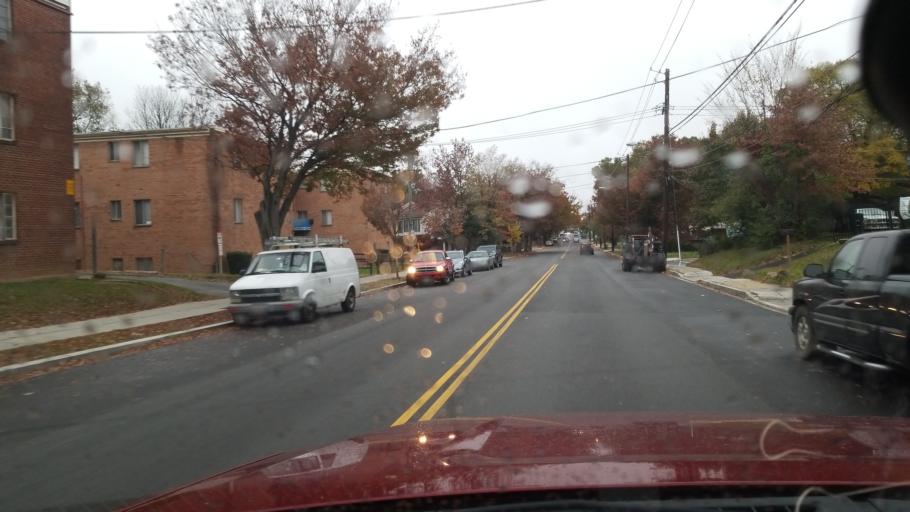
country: US
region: Maryland
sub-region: Prince George's County
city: Fairmount Heights
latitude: 38.9067
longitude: -76.9269
